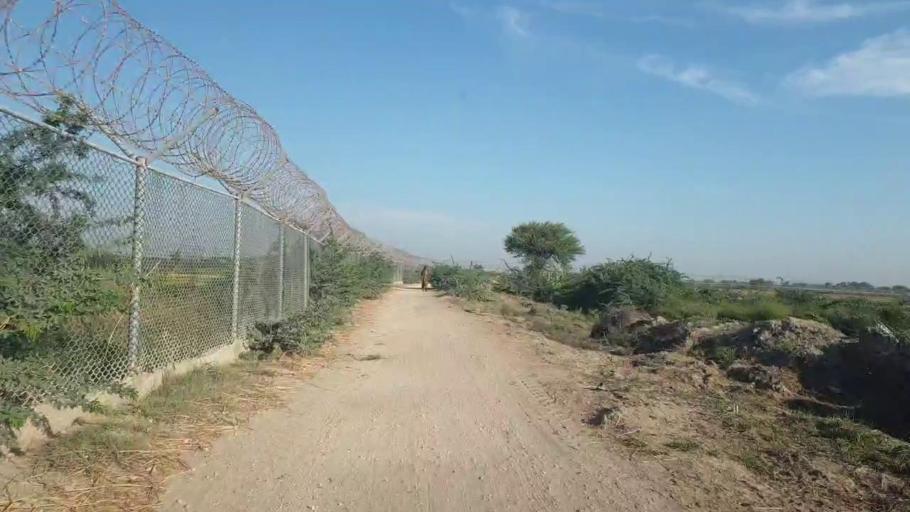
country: PK
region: Sindh
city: Talhar
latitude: 24.8481
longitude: 68.8571
